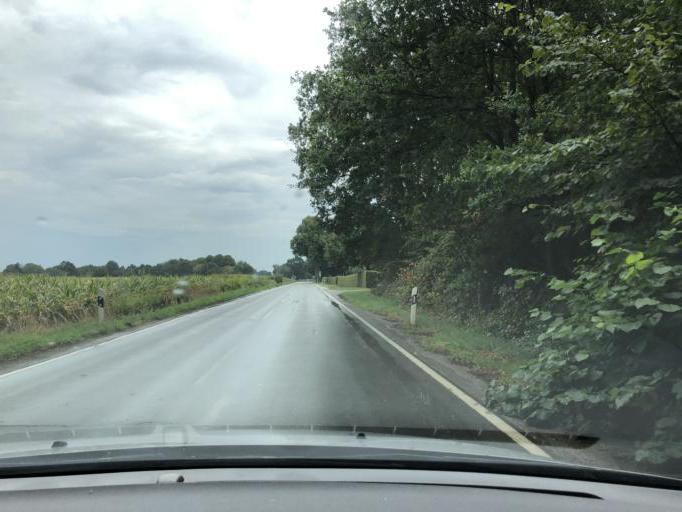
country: DE
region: North Rhine-Westphalia
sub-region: Regierungsbezirk Dusseldorf
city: Schermbeck
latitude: 51.6293
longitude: 6.9002
